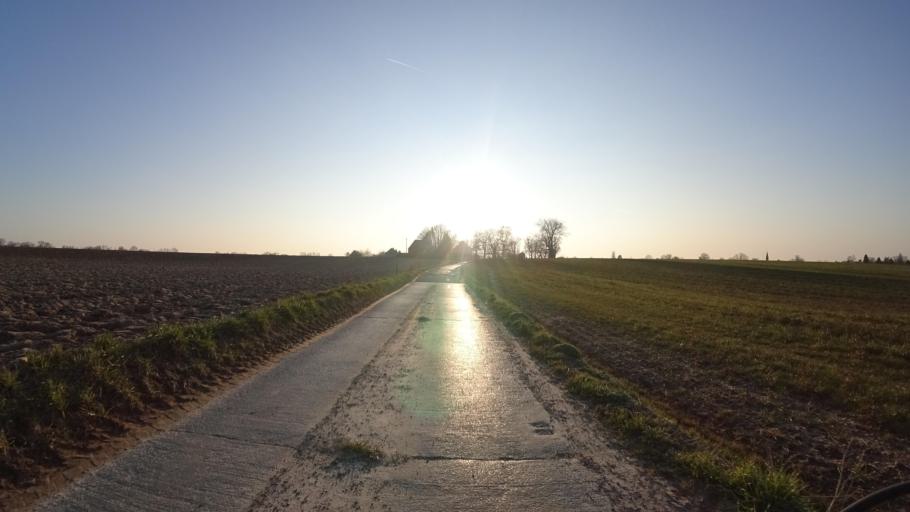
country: BE
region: Wallonia
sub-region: Province du Brabant Wallon
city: Chastre
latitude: 50.5836
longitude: 4.6520
